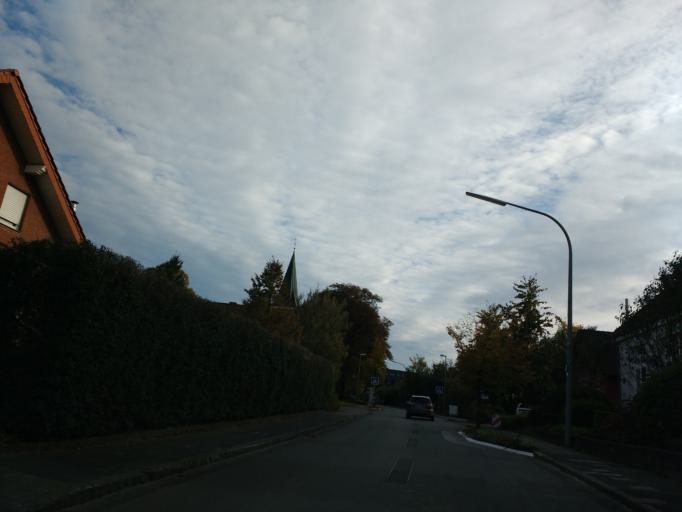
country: DE
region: North Rhine-Westphalia
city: Lichtenau
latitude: 51.6705
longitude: 8.8344
